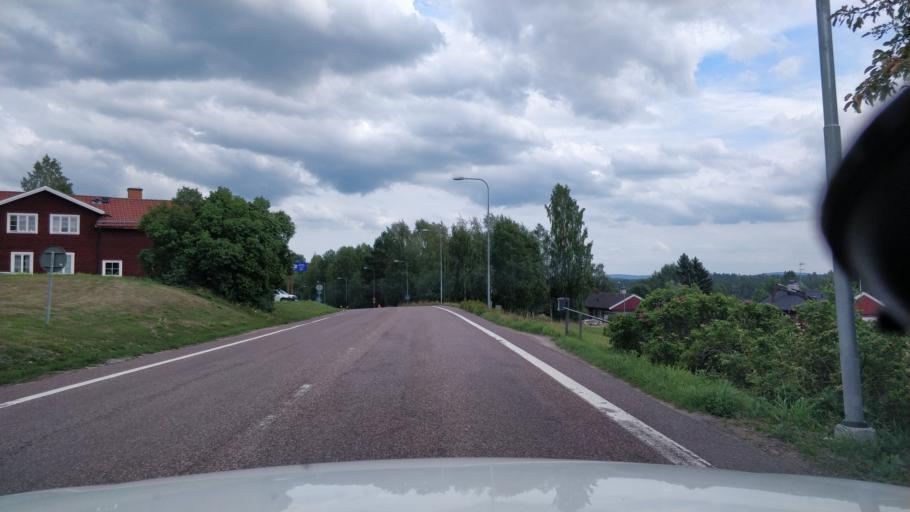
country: SE
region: Dalarna
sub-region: Faluns Kommun
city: Bjursas
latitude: 60.7372
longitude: 15.4508
